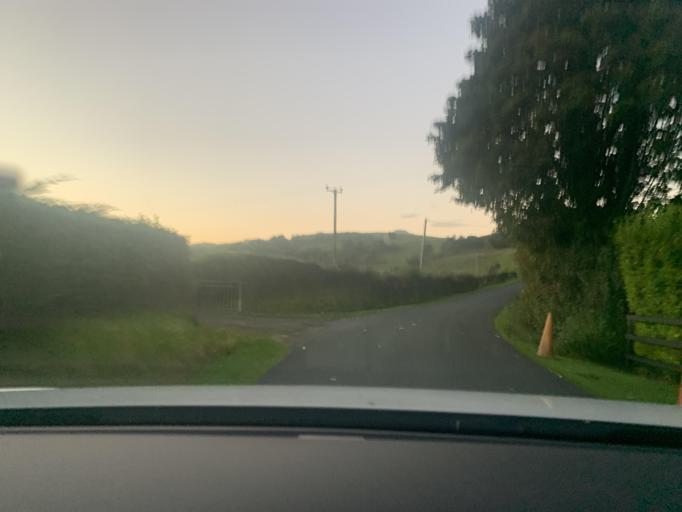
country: IE
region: Connaught
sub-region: County Leitrim
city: Manorhamilton
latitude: 54.2728
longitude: -8.2840
